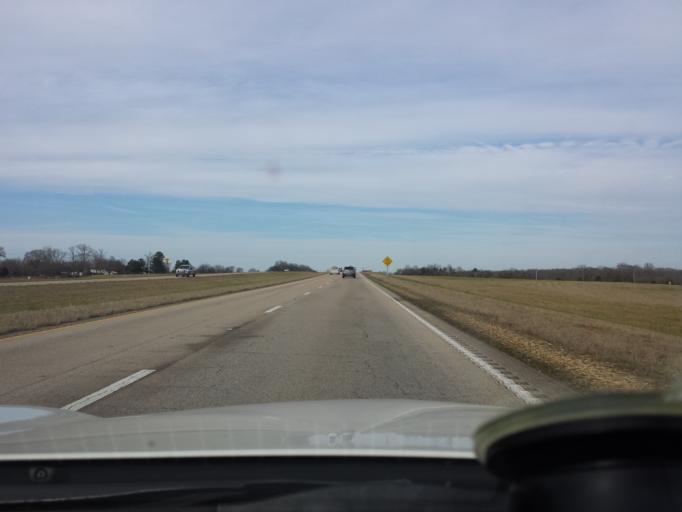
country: US
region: Mississippi
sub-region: Chickasaw County
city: Okolona
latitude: 33.9981
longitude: -88.7014
